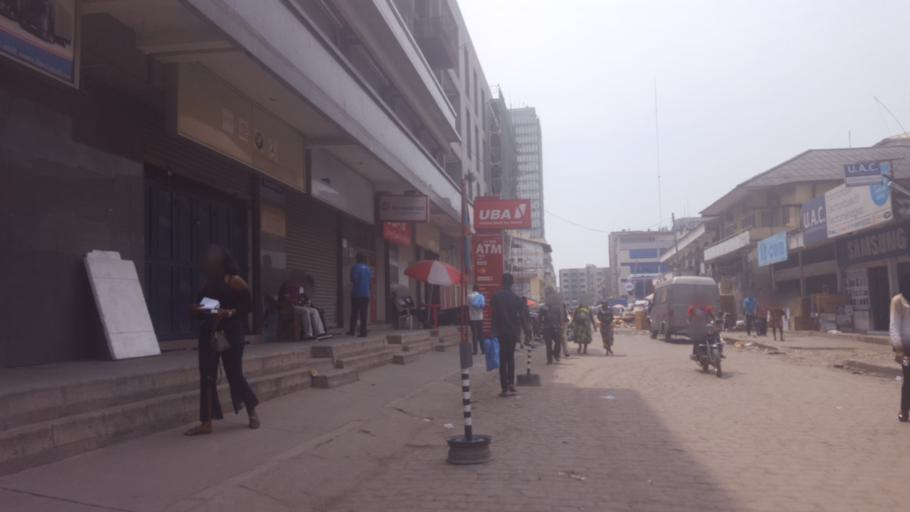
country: CD
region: Kinshasa
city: Kinshasa
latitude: -4.3060
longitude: 15.3115
